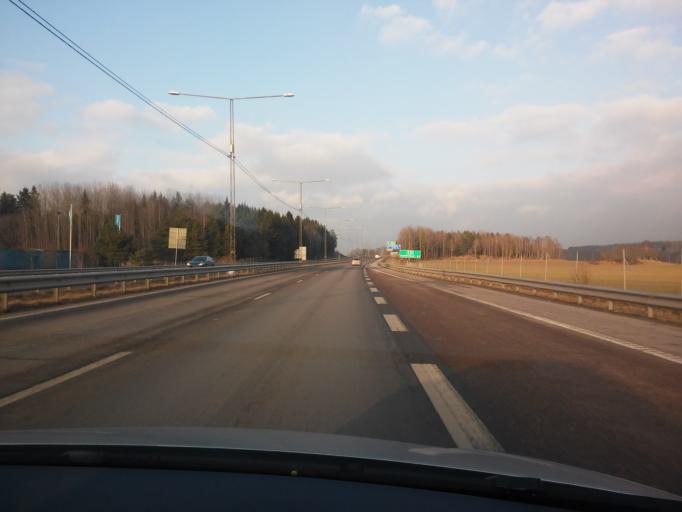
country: SE
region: Stockholm
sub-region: Taby Kommun
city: Taby
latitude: 59.4595
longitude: 18.1411
